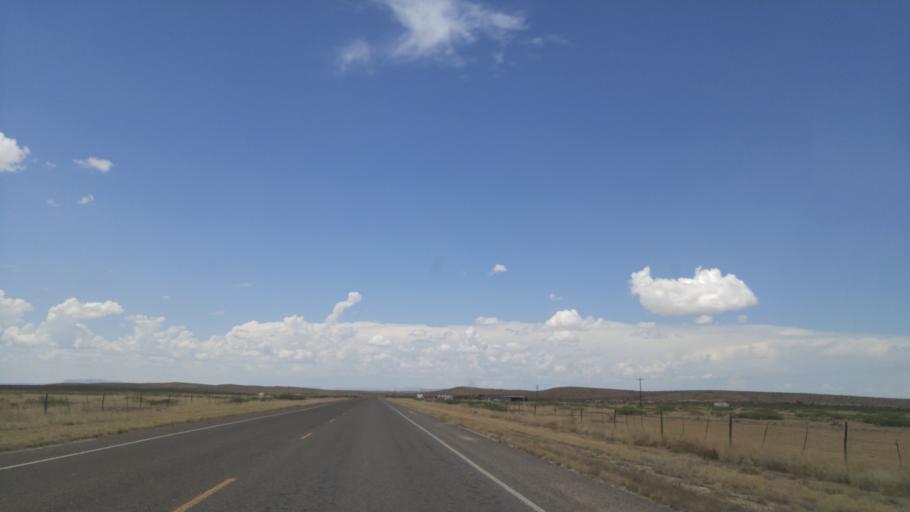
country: US
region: Texas
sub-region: Brewster County
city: Alpine
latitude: 29.5815
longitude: -103.5569
